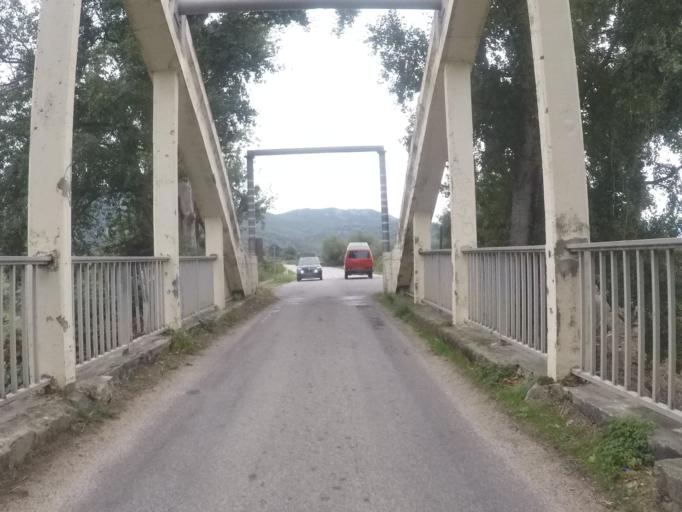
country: FR
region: Corsica
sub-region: Departement de la Corse-du-Sud
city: Propriano
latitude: 41.7264
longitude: 8.8288
